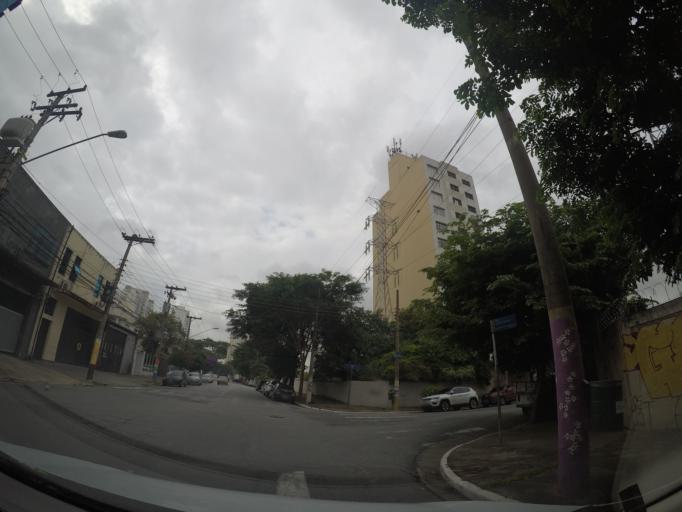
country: BR
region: Sao Paulo
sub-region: Sao Paulo
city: Sao Paulo
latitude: -23.5592
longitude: -46.6036
